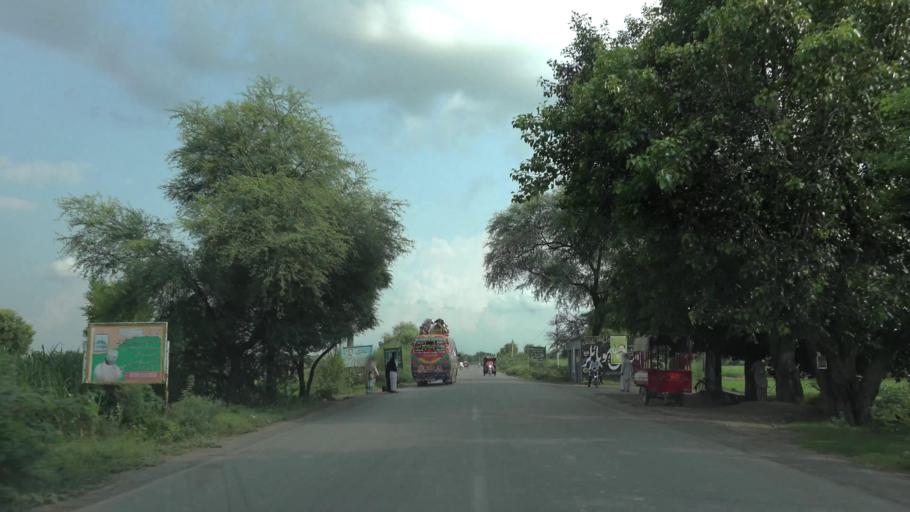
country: PK
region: Punjab
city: Nankana Sahib
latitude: 31.4883
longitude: 73.6076
